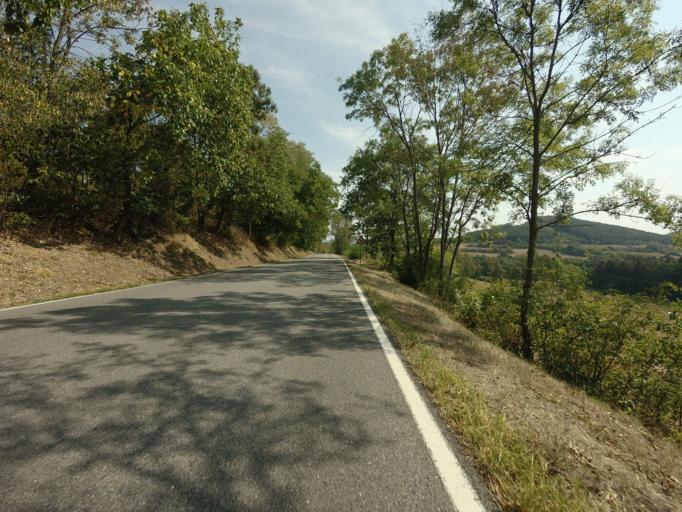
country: CZ
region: Central Bohemia
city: Petrovice
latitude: 49.5871
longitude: 14.3817
